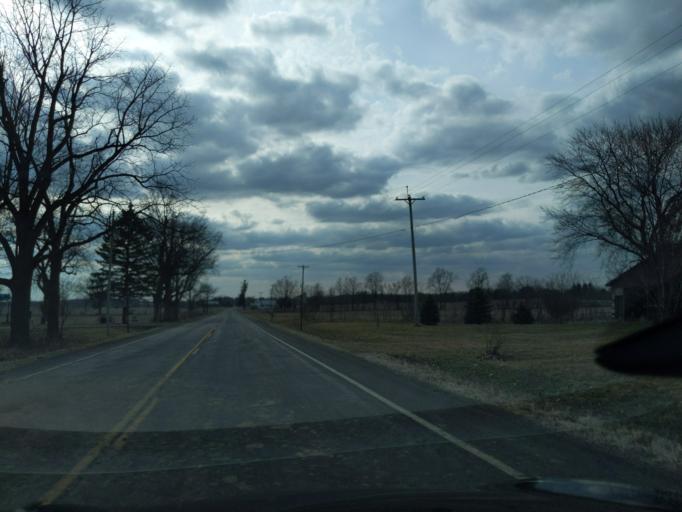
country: US
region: Michigan
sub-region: Ingham County
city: Mason
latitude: 42.5240
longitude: -84.4738
